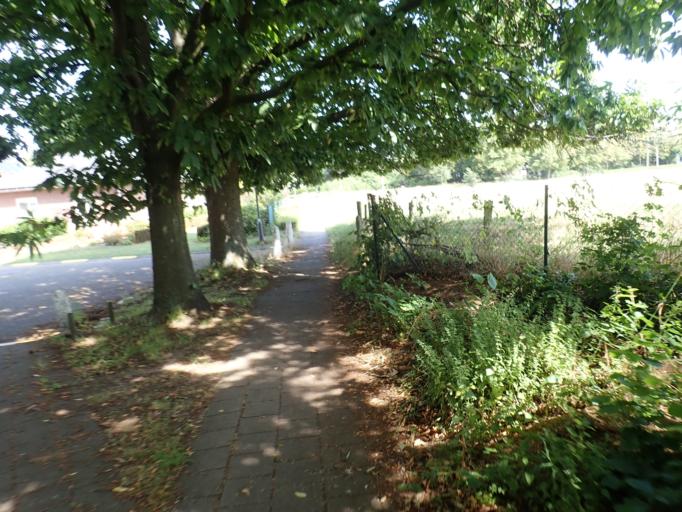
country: BE
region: Flanders
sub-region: Provincie Antwerpen
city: Borsbeek
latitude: 51.2082
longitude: 4.4958
